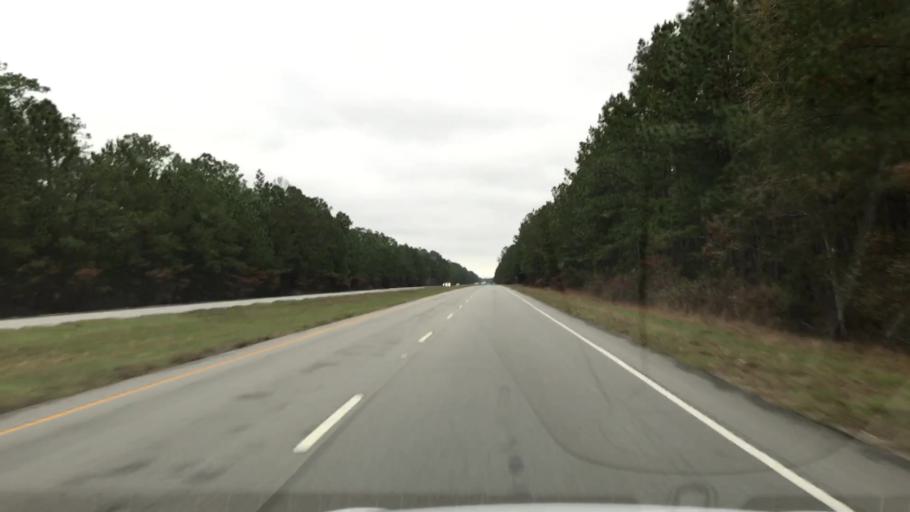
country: US
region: South Carolina
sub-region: Charleston County
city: Awendaw
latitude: 33.1526
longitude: -79.4315
